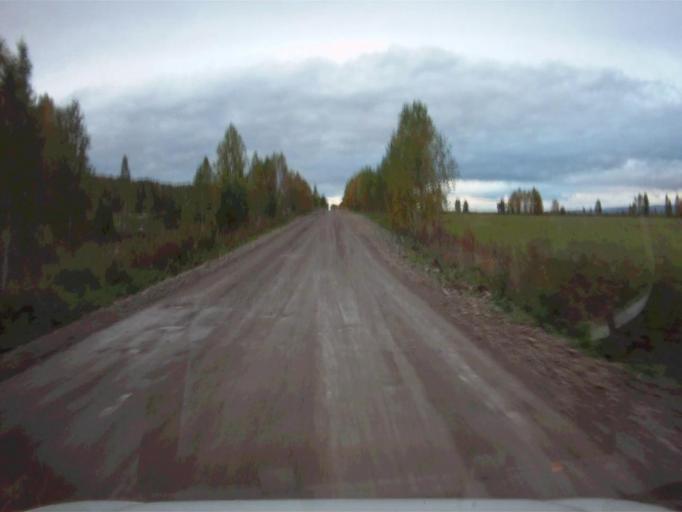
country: RU
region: Sverdlovsk
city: Mikhaylovsk
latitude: 56.1969
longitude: 59.1994
